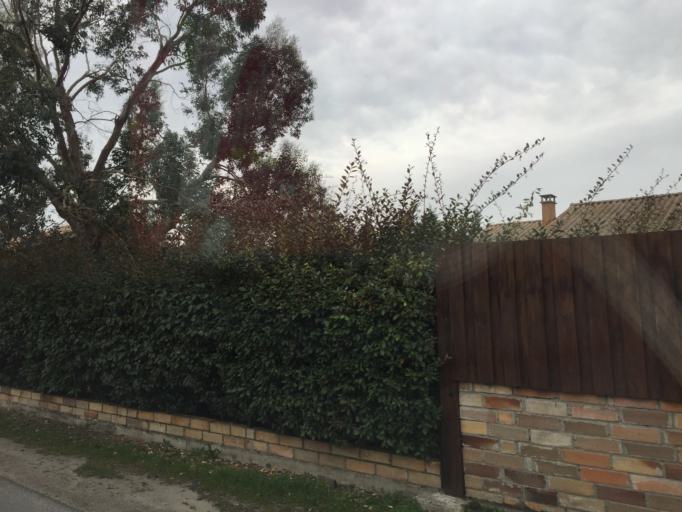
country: FR
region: Aquitaine
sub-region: Departement de la Gironde
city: Carcans
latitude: 45.0783
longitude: -1.0491
